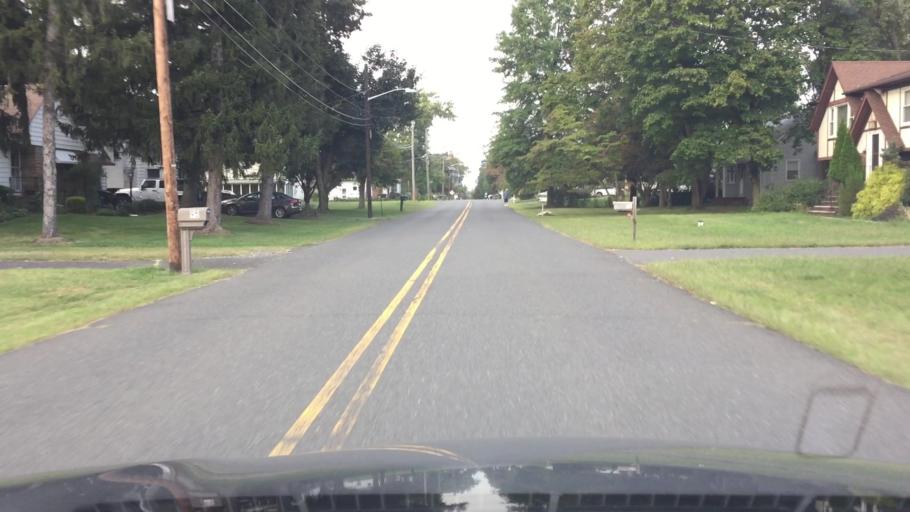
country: US
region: New Jersey
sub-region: Somerset County
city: Somerset
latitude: 40.5232
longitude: -74.5039
